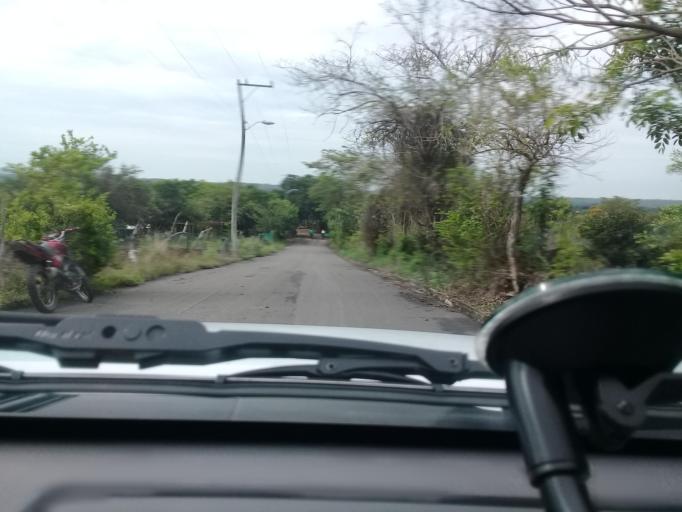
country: MX
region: Veracruz
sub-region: Puente Nacional
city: Cabezas
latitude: 19.3339
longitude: -96.3861
